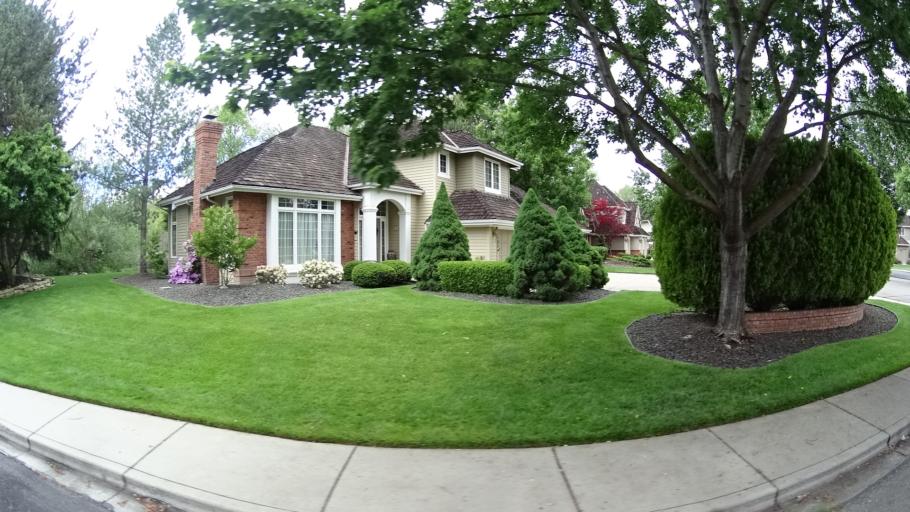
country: US
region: Idaho
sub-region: Ada County
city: Eagle
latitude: 43.6683
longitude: -116.2915
